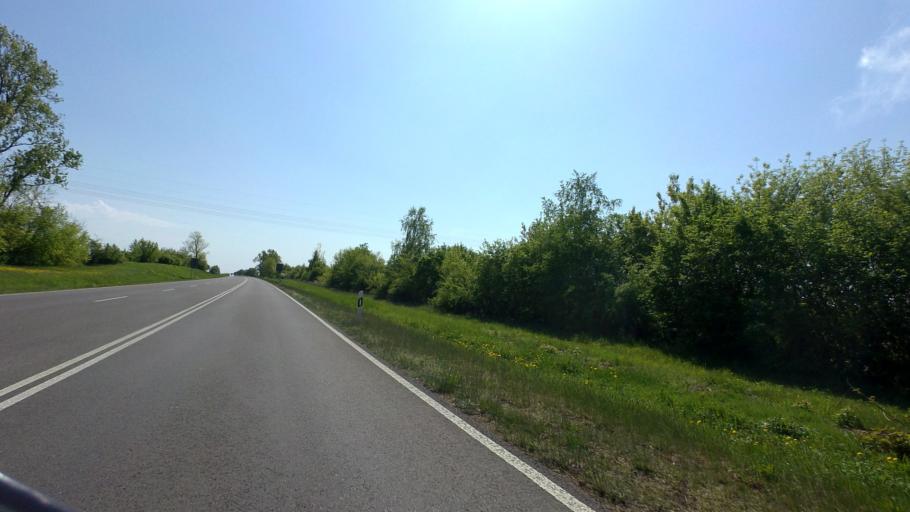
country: DE
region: Brandenburg
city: Beeskow
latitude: 52.1825
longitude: 14.2170
